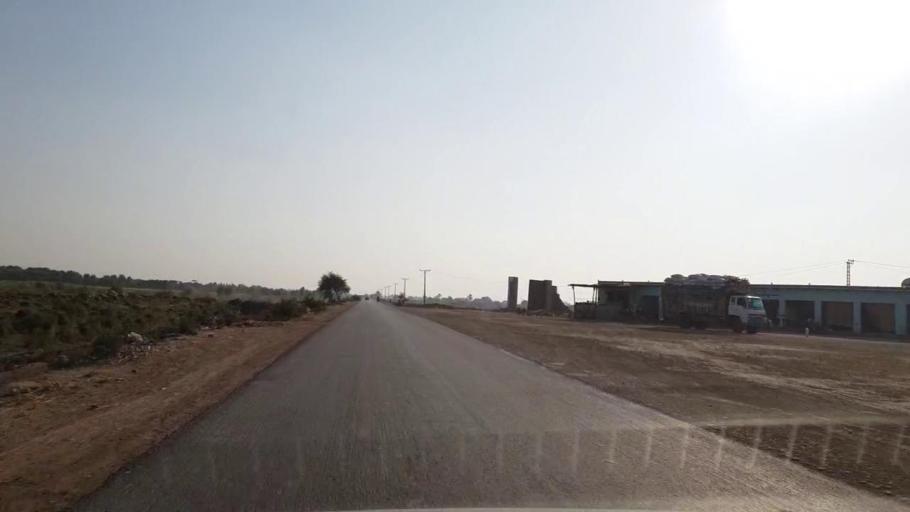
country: PK
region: Sindh
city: Bulri
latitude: 24.9048
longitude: 68.3469
